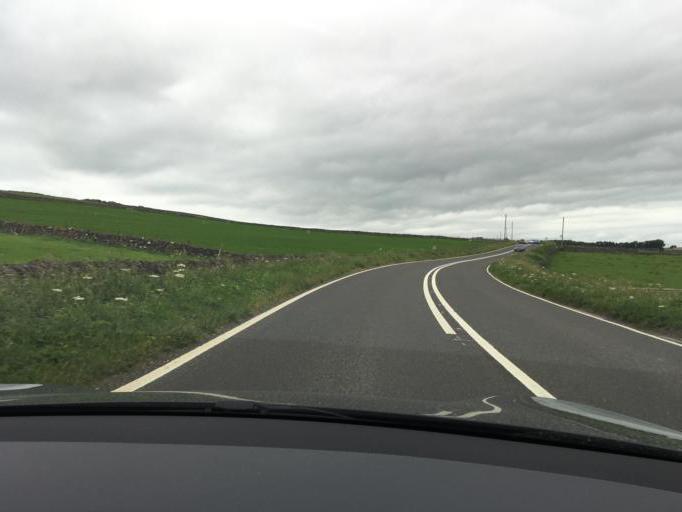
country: GB
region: England
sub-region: Derbyshire
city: Tideswell
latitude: 53.2805
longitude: -1.7484
